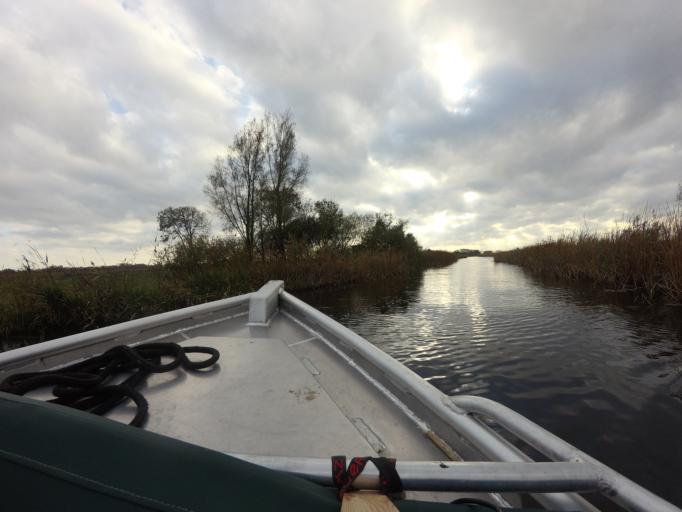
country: NL
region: Overijssel
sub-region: Gemeente Steenwijkerland
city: Blokzijl
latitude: 52.7546
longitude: 5.9663
